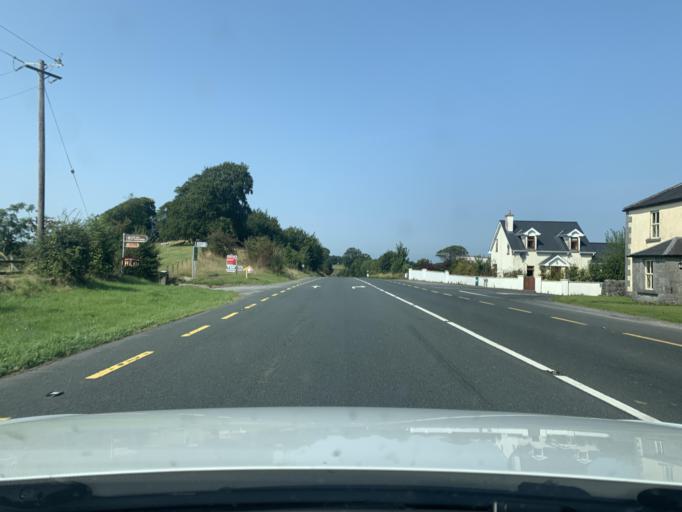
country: IE
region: Leinster
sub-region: An Iarmhi
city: Athlone
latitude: 53.4911
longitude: -8.0336
